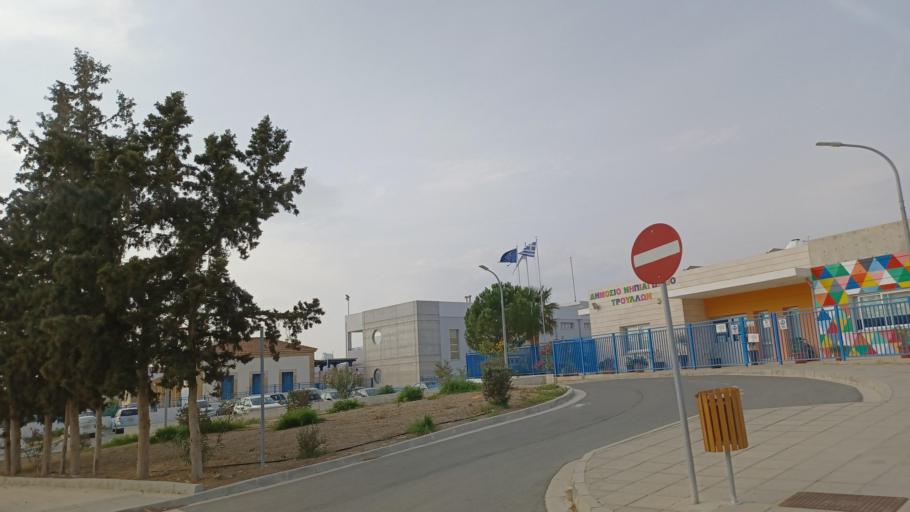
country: CY
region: Larnaka
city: Troulloi
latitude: 35.0298
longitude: 33.6131
